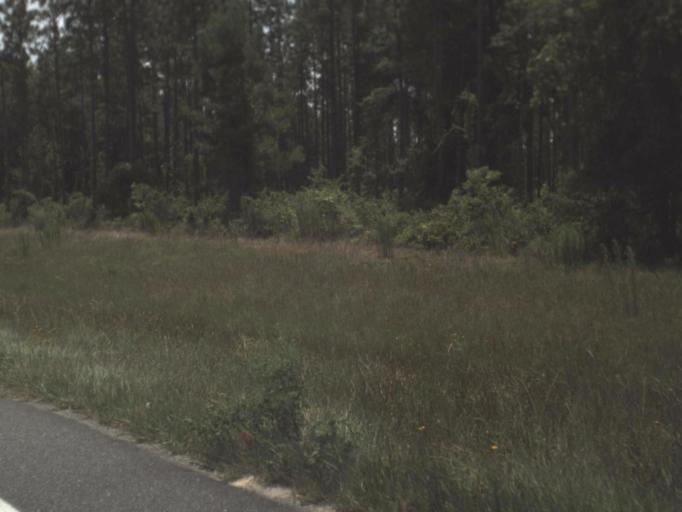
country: US
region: Florida
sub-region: Madison County
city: Madison
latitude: 30.4007
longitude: -83.2107
